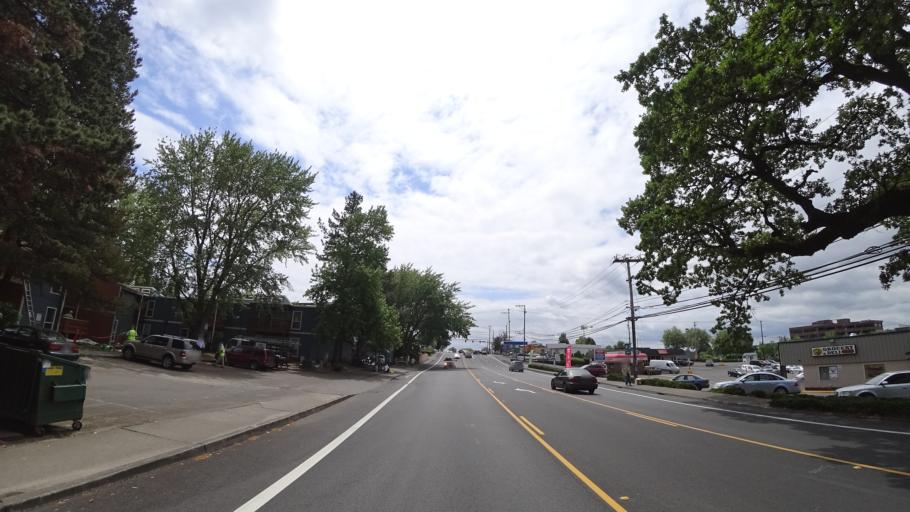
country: US
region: Oregon
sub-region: Washington County
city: Garden Home-Whitford
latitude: 45.4583
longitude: -122.7816
